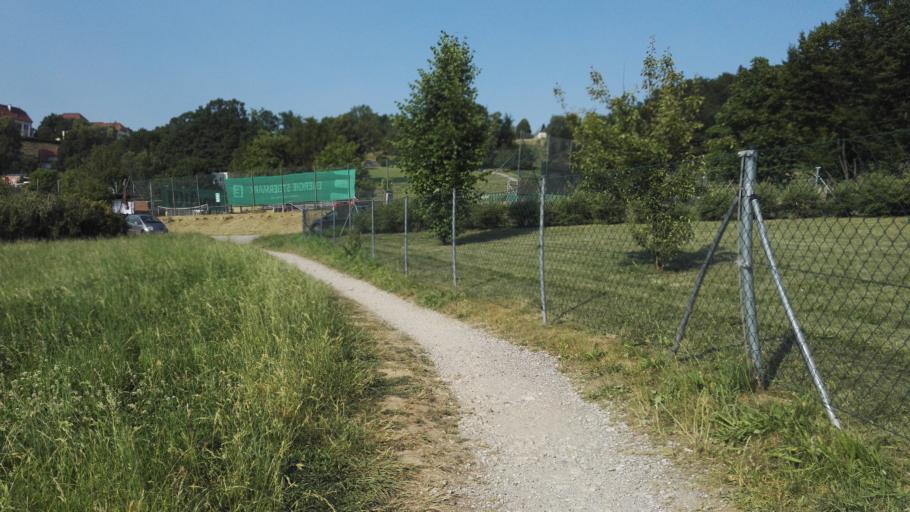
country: AT
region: Styria
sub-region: Graz Stadt
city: Mariatrost
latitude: 47.1034
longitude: 15.4896
